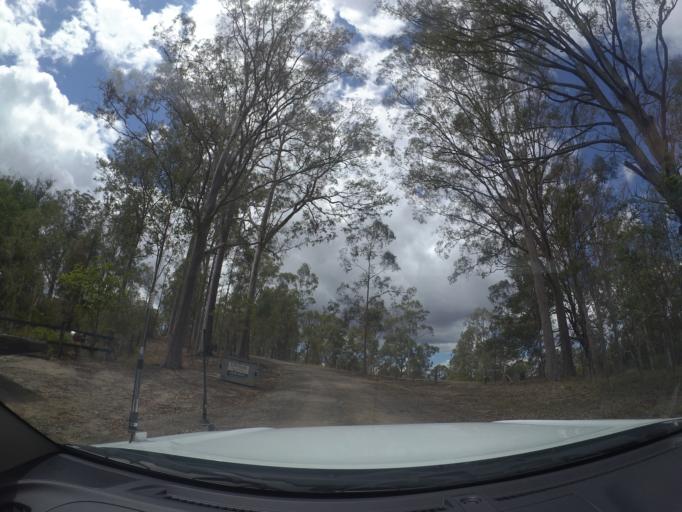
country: AU
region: Queensland
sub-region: Logan
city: Cedar Vale
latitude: -27.9171
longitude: 153.0358
